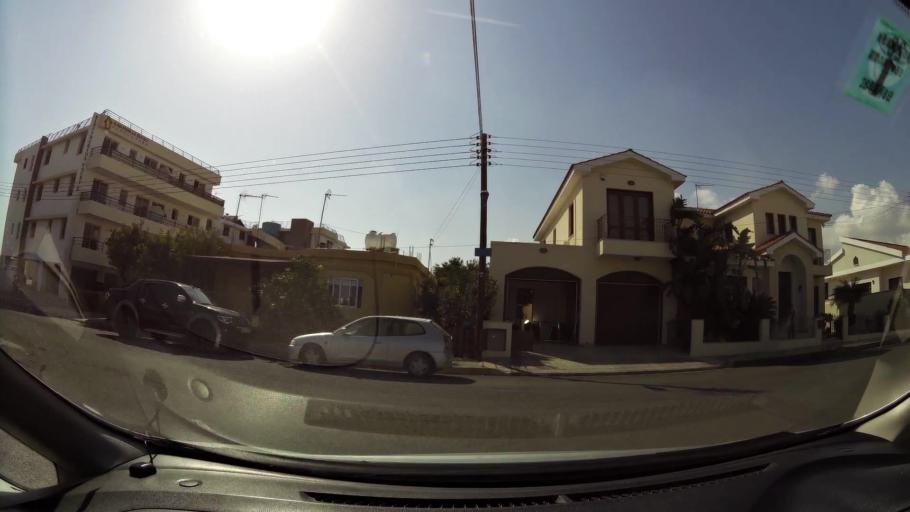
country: CY
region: Larnaka
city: Aradippou
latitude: 34.9507
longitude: 33.5846
